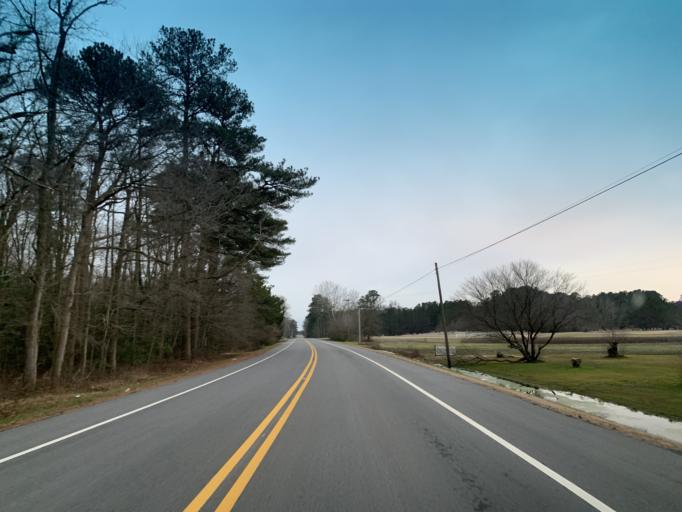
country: US
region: Maryland
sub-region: Worcester County
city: Pocomoke City
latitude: 38.0781
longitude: -75.5447
